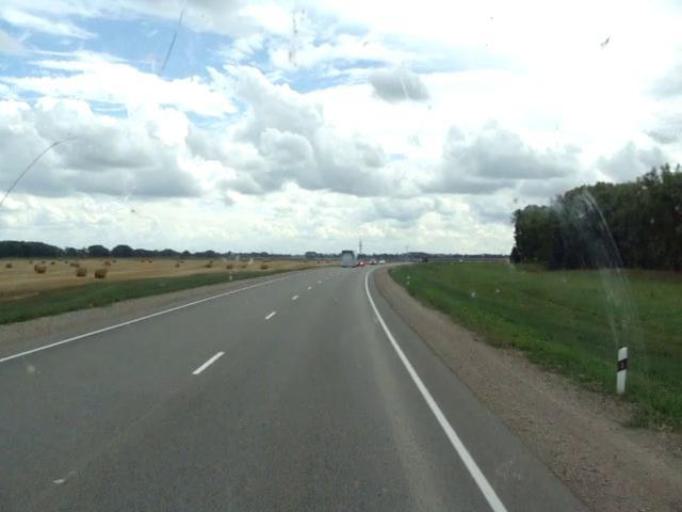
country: RU
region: Altai Krai
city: Shubenka
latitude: 52.6830
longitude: 85.0455
